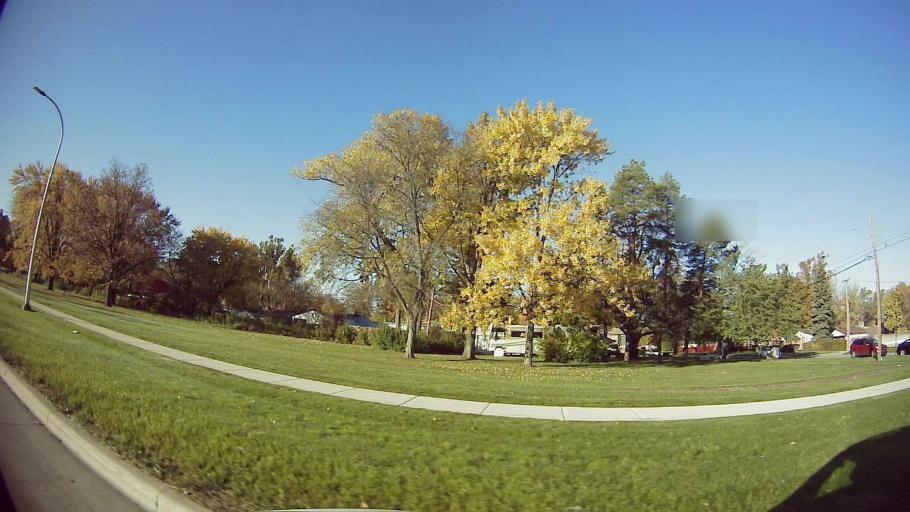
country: US
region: Michigan
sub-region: Oakland County
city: Oak Park
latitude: 42.4521
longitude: -83.1816
